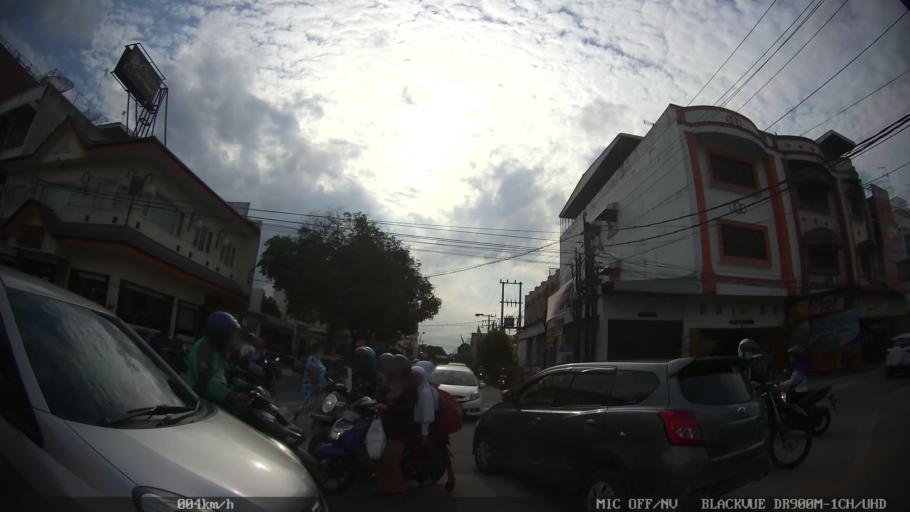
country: ID
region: North Sumatra
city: Medan
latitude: 3.6138
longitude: 98.6806
